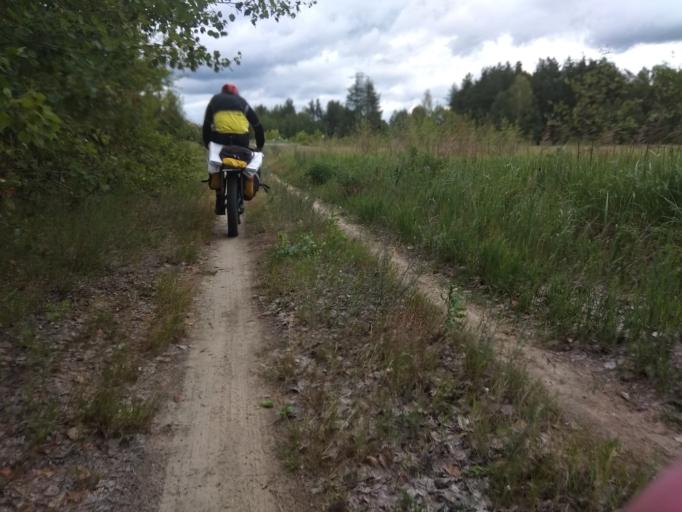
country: RU
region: Moskovskaya
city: Kerva
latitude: 55.5776
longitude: 39.6870
